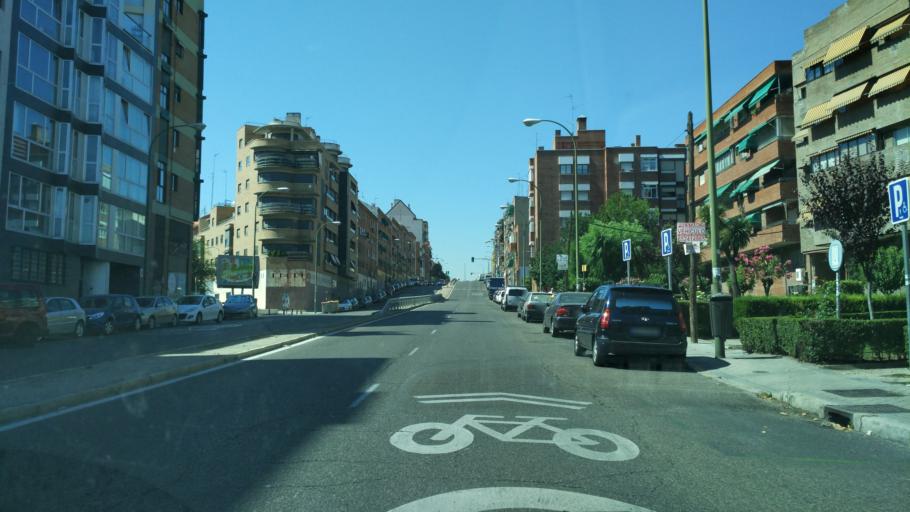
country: ES
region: Madrid
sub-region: Provincia de Madrid
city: Tetuan de las Victorias
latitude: 40.4608
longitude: -3.7094
